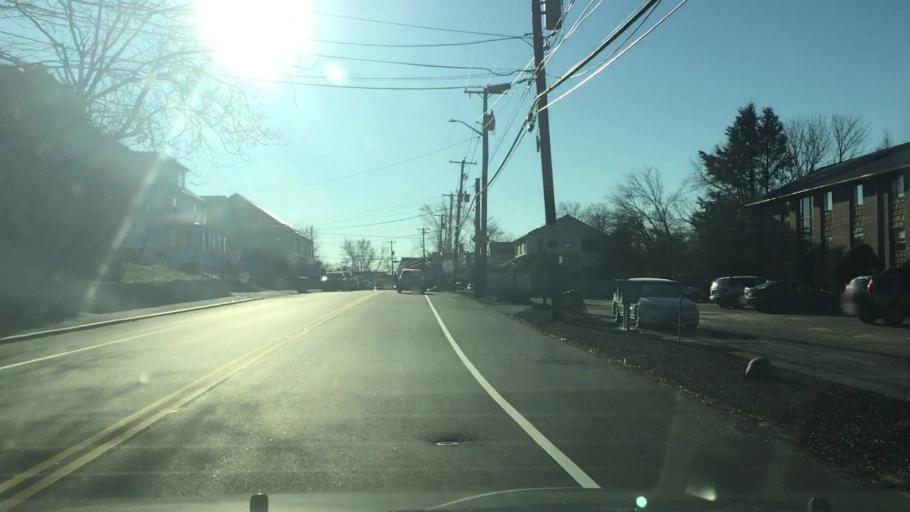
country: US
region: Massachusetts
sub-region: Middlesex County
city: Lowell
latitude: 42.6576
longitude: -71.3418
